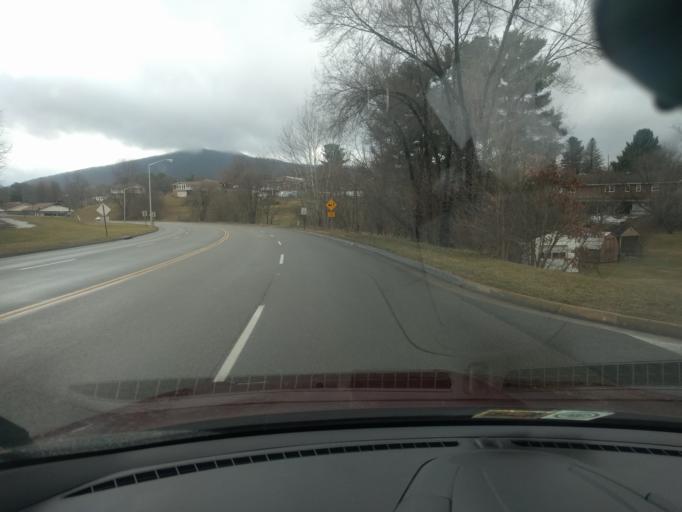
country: US
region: Virginia
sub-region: Pulaski County
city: Pulaski
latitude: 37.0576
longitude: -80.7555
